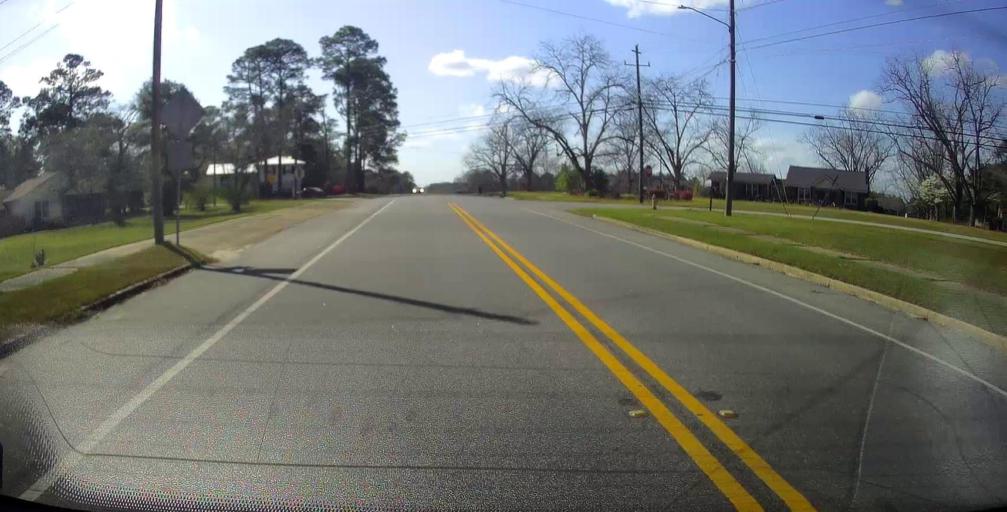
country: US
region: Georgia
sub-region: Dodge County
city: Eastman
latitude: 32.1963
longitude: -83.1866
